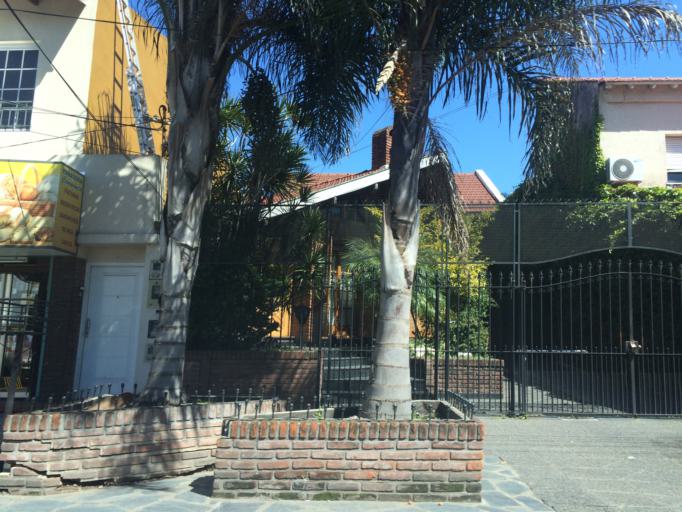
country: AR
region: Buenos Aires
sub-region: Partido de Lomas de Zamora
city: Lomas de Zamora
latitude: -34.7351
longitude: -58.3960
